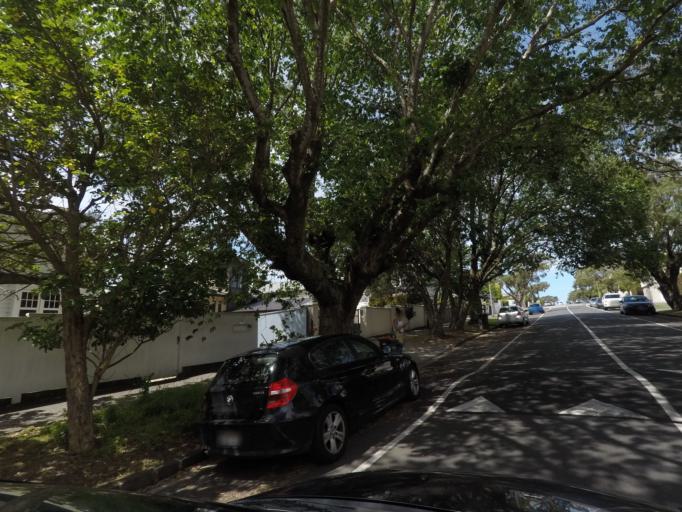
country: NZ
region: Auckland
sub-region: Auckland
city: Auckland
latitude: -36.8419
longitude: 174.7339
